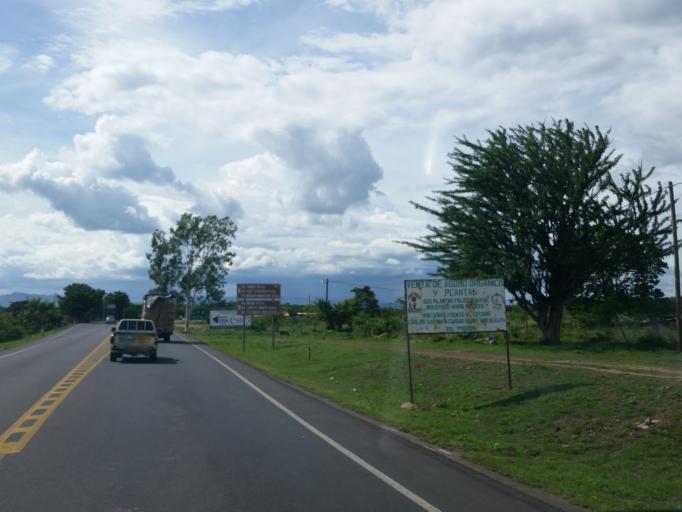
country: NI
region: Matagalpa
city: Ciudad Dario
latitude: 12.7293
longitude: -86.1114
